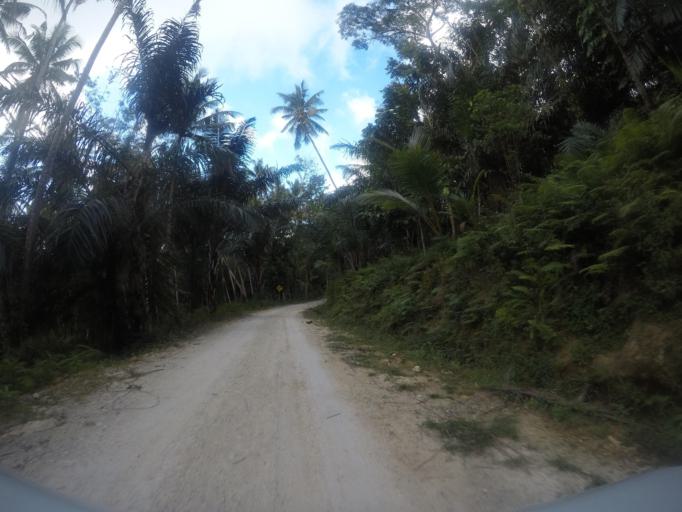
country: TL
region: Lautem
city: Lospalos
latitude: -8.5290
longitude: 126.9340
